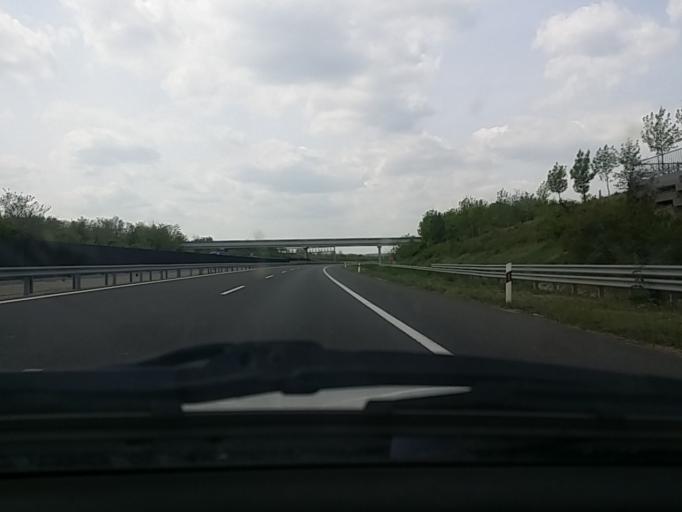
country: HU
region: Somogy
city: Balatonszarszo
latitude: 46.8142
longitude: 17.8487
